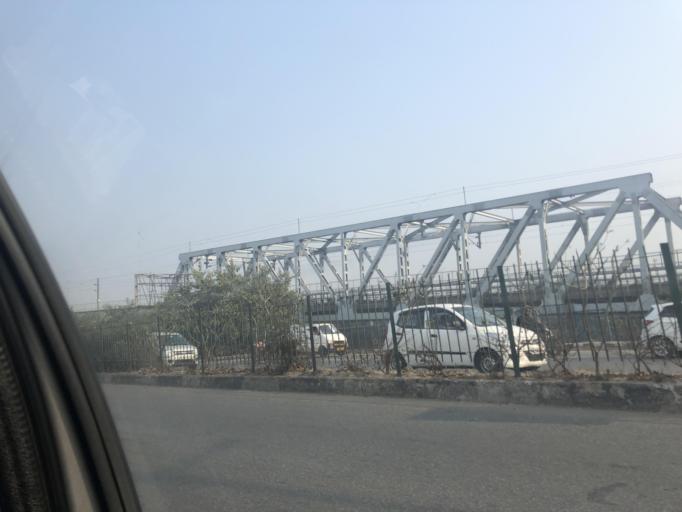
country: IN
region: NCT
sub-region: North West Delhi
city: Pitampura
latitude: 28.6314
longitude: 77.1323
